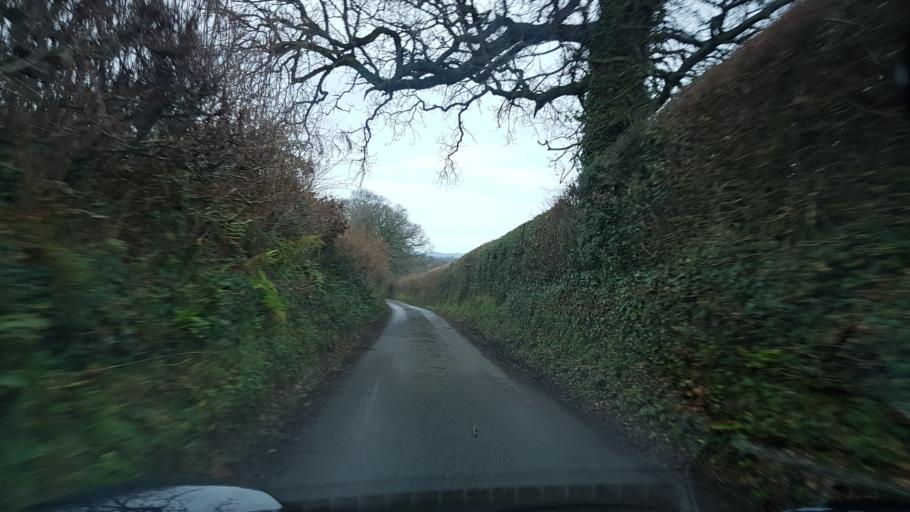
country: GB
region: England
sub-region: Somerset
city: Chard
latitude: 50.9097
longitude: -2.9639
